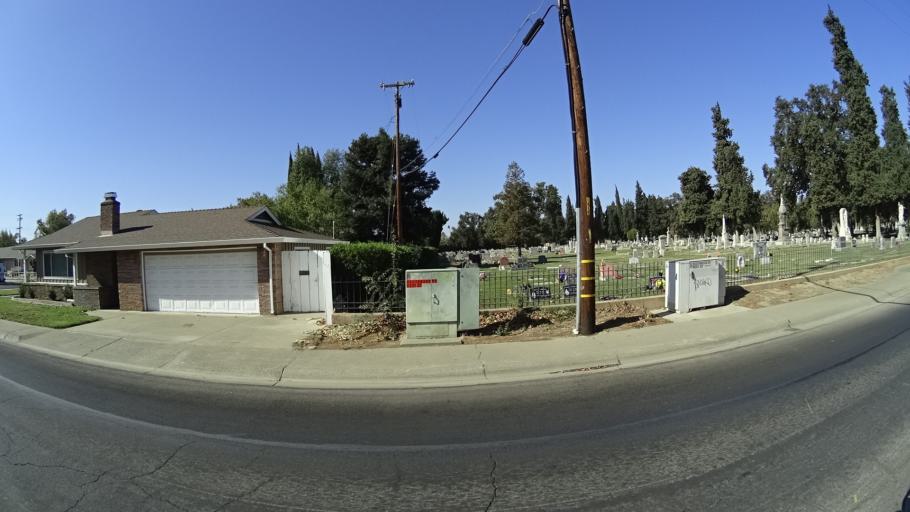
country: US
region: California
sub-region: Yolo County
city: Woodland
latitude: 38.6691
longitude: -121.7841
